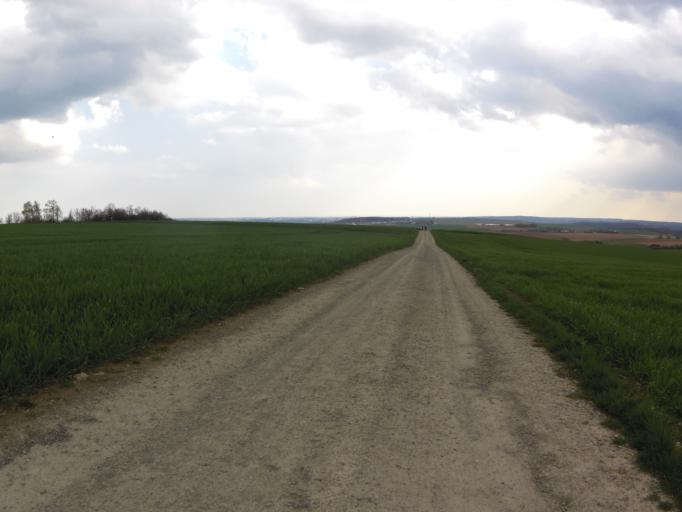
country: DE
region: Bavaria
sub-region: Regierungsbezirk Unterfranken
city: Rimpar
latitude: 49.8674
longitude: 9.9481
